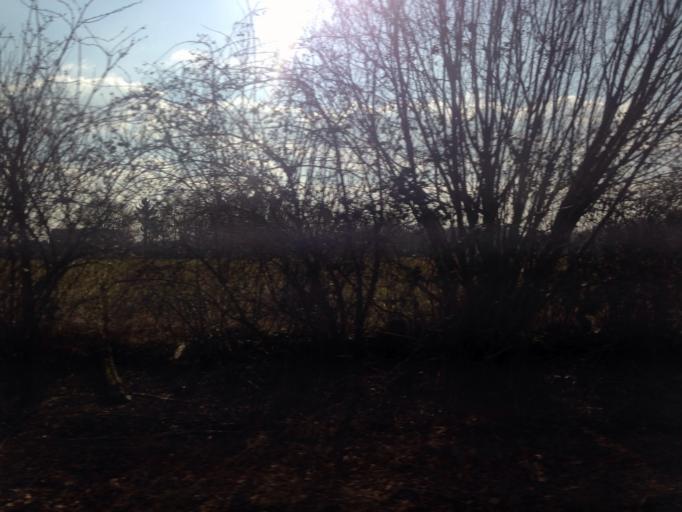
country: DE
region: North Rhine-Westphalia
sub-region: Regierungsbezirk Munster
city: Muenster
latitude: 52.0146
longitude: 7.5883
